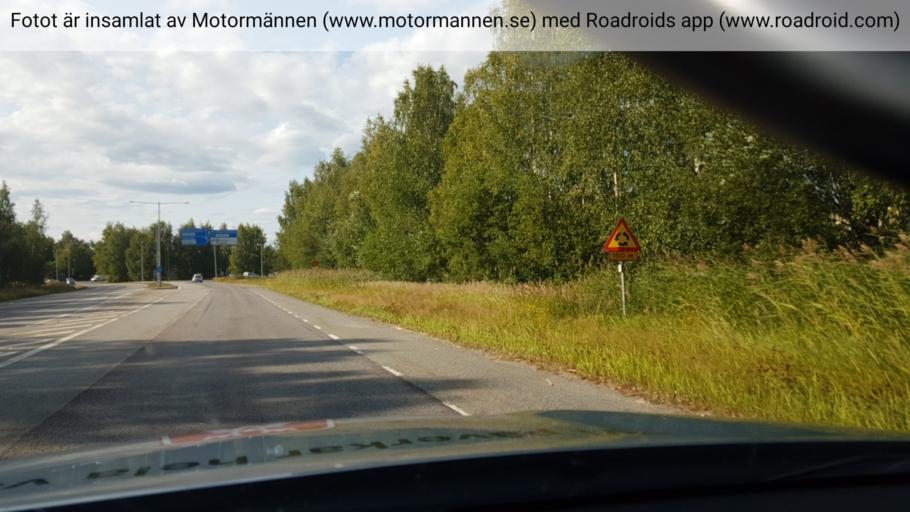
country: SE
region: Norrbotten
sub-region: Pitea Kommun
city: Pitea
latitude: 65.3090
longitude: 21.5006
